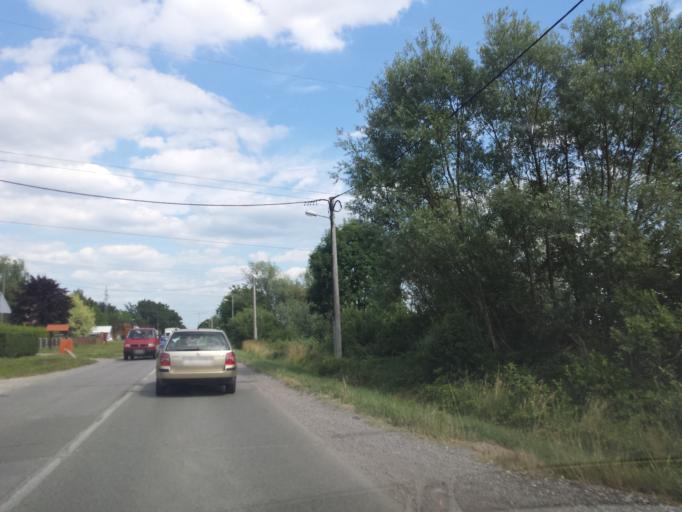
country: HR
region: Grad Zagreb
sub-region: Sesvete
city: Sesvete
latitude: 45.8139
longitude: 16.1869
